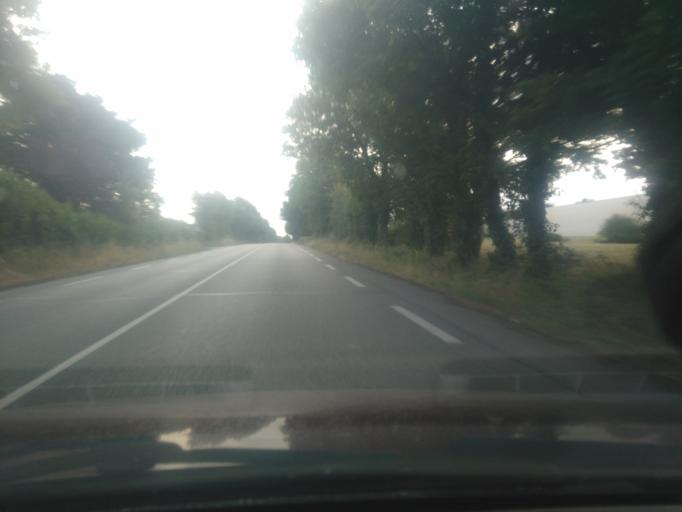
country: FR
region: Pays de la Loire
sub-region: Departement de la Vendee
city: Les Essarts
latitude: 46.7885
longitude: -1.1853
